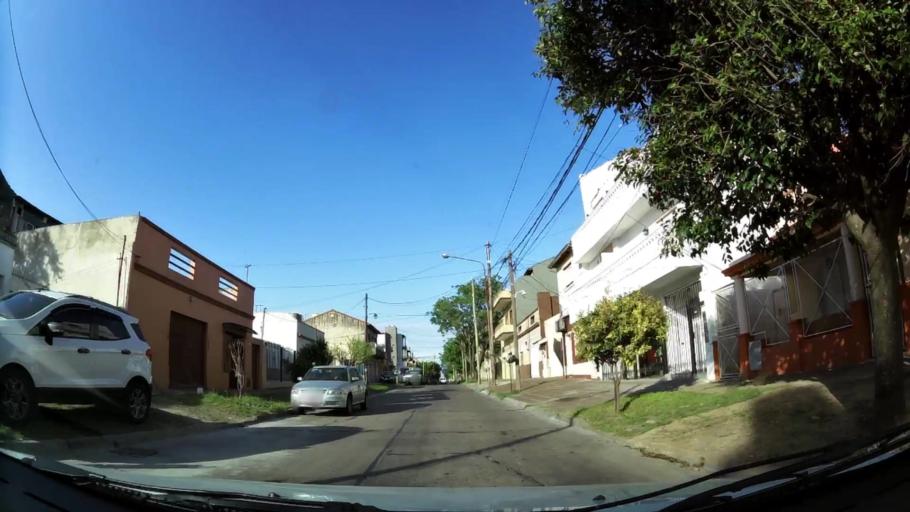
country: AR
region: Buenos Aires
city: Caseros
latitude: -34.5852
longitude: -58.5851
